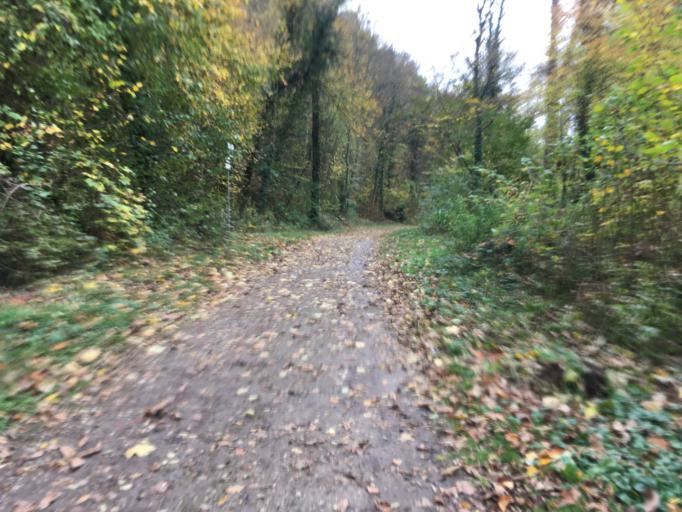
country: DE
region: Baden-Wuerttemberg
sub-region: Freiburg Region
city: Sasbach
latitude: 48.1087
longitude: 7.5893
